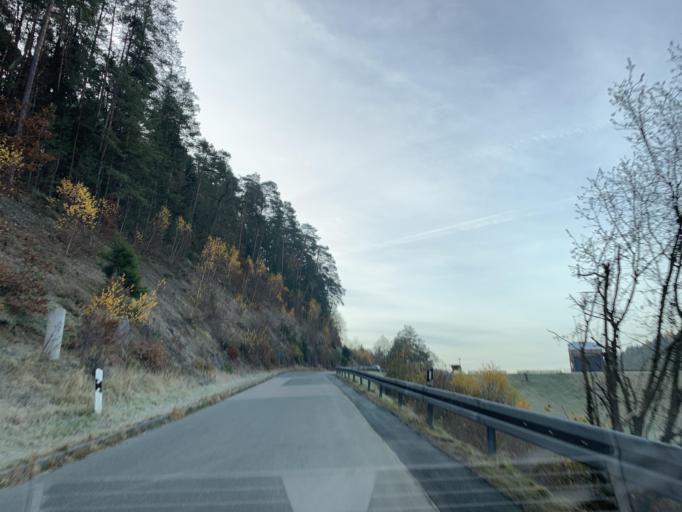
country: DE
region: Bavaria
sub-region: Upper Palatinate
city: Thanstein
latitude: 49.3585
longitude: 12.4488
